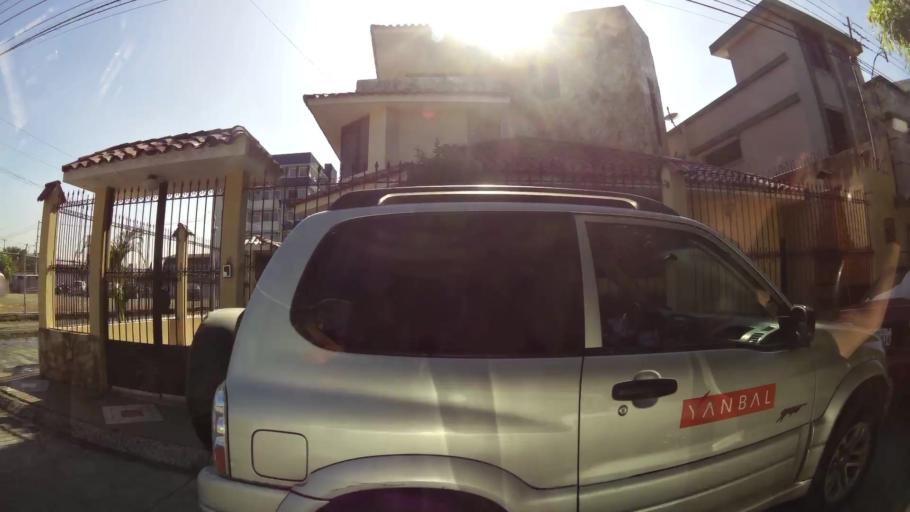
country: EC
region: Guayas
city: Eloy Alfaro
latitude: -2.1536
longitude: -79.9005
